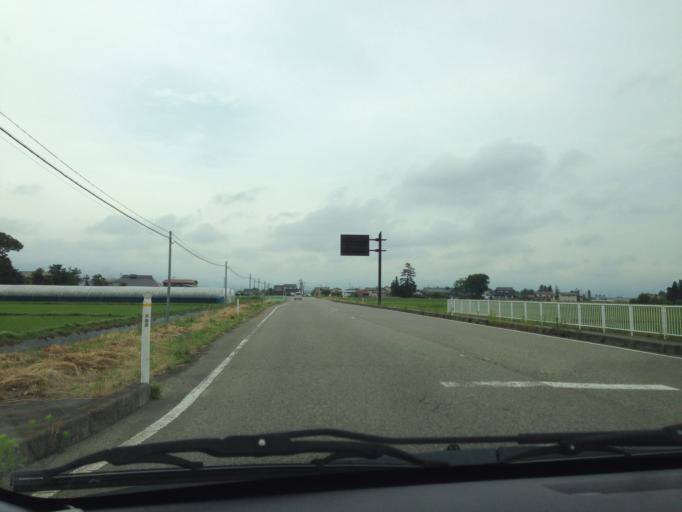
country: JP
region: Fukushima
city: Kitakata
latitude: 37.5642
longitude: 139.8888
